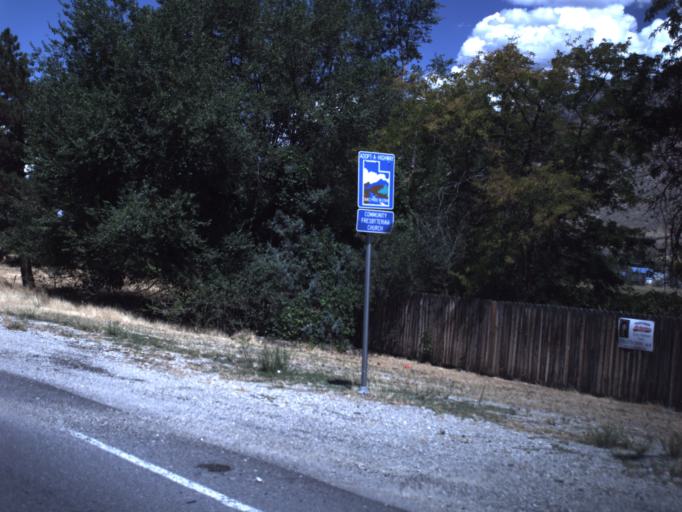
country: US
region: Utah
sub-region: Box Elder County
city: Brigham City
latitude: 41.5287
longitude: -112.0165
